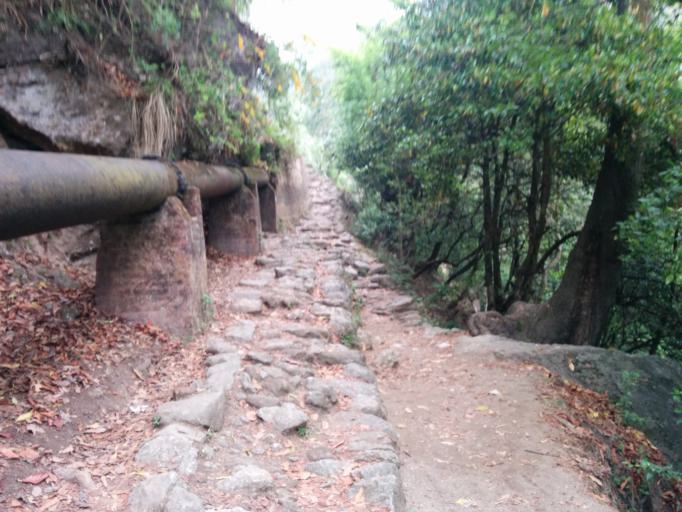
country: NP
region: Central Region
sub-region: Bagmati Zone
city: Bhaktapur
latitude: 27.7650
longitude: 85.4235
